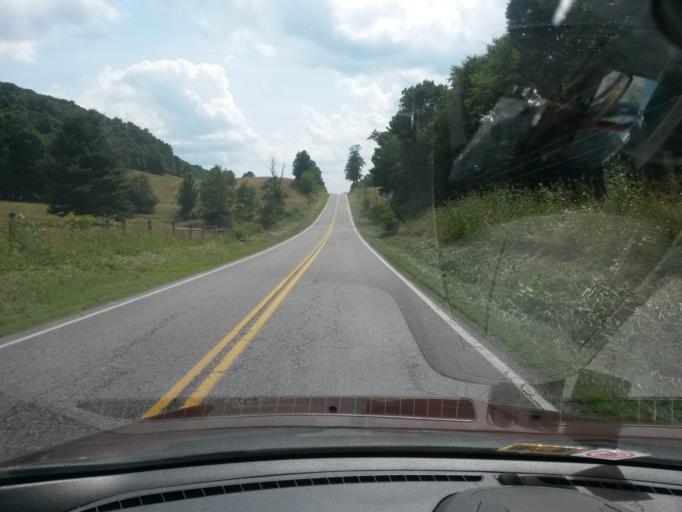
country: US
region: Virginia
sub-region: Highland County
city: Monterey
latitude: 38.4363
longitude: -79.5480
